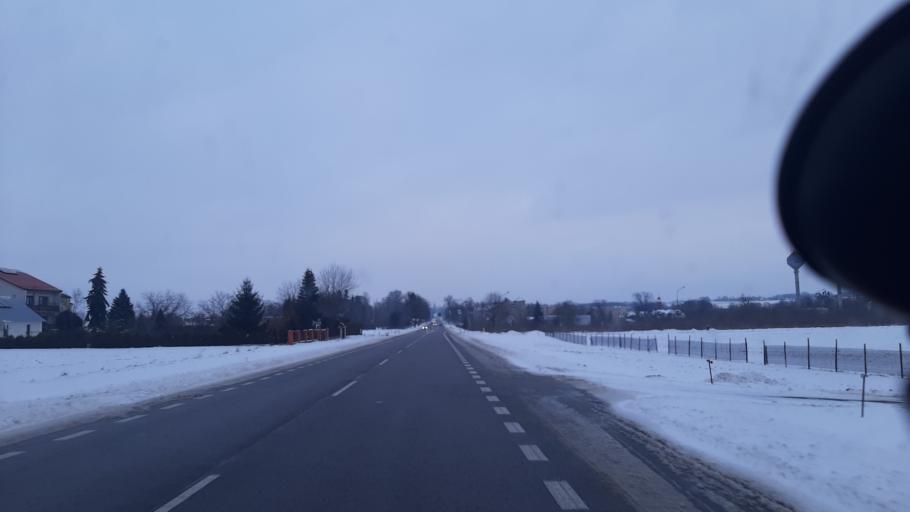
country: PL
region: Lublin Voivodeship
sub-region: Powiat pulawski
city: Markuszow
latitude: 51.3666
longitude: 22.2901
